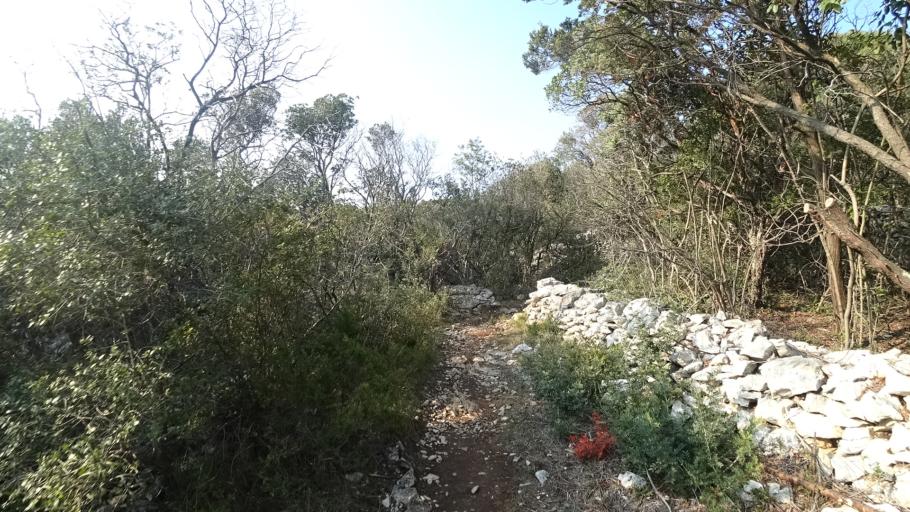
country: HR
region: Primorsko-Goranska
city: Mali Losinj
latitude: 44.5120
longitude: 14.4811
